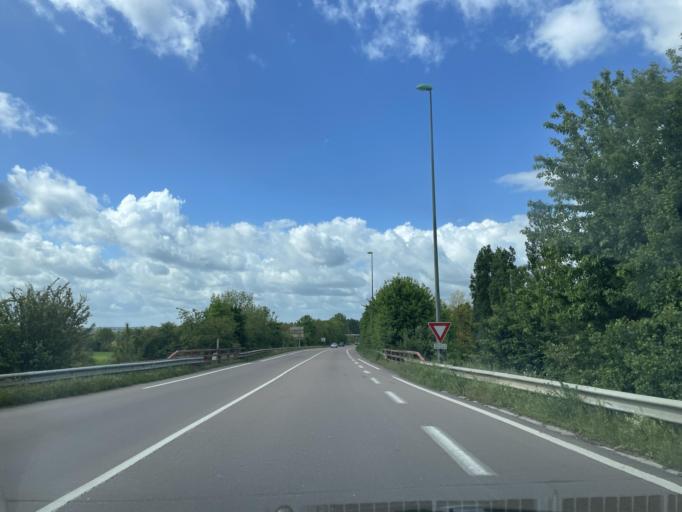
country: FR
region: Bourgogne
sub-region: Departement de l'Yonne
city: Maillot
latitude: 48.1891
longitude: 3.3104
